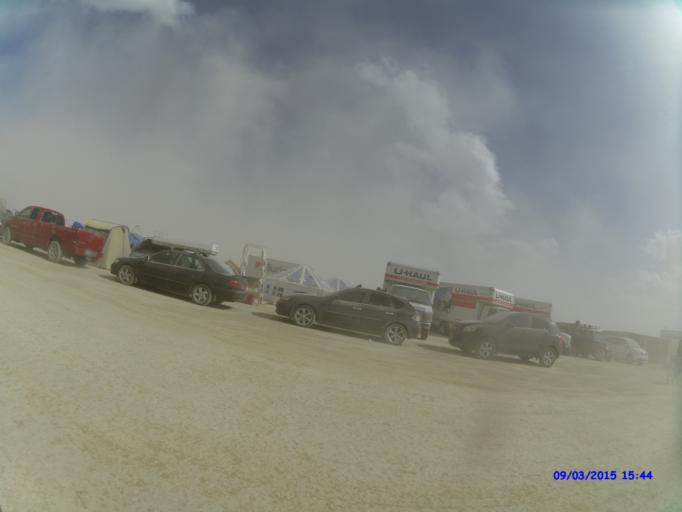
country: US
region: Nevada
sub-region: Pershing County
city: Lovelock
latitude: 40.7939
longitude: -119.2140
